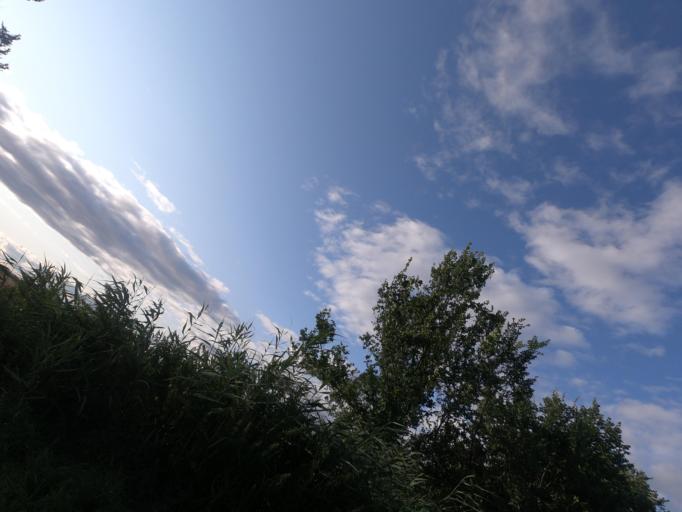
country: HU
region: Heves
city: Szihalom
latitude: 47.7197
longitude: 20.5612
